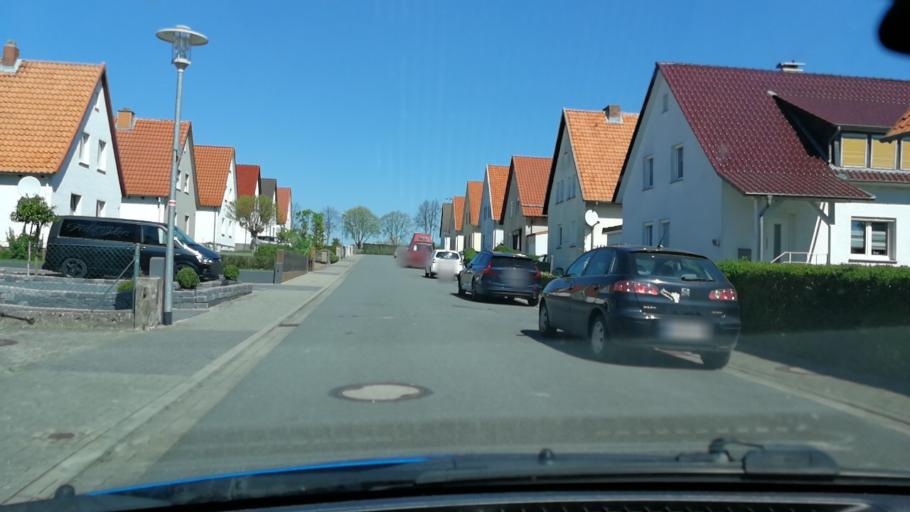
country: DE
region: Lower Saxony
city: Hillerse
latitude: 51.6983
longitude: 9.9594
